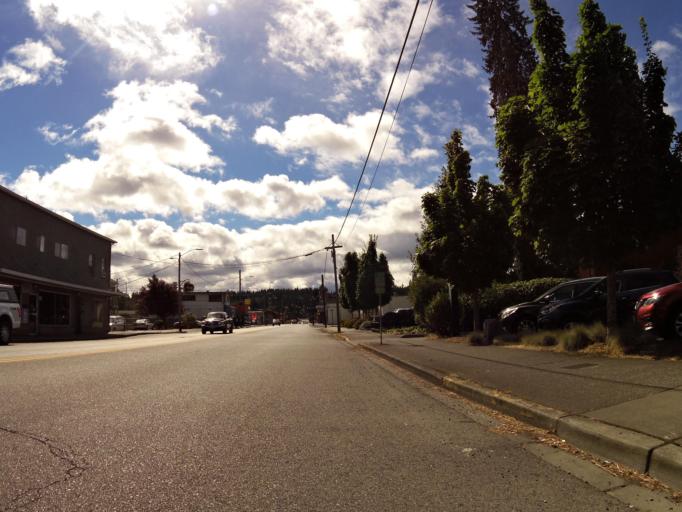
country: US
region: Washington
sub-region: Mason County
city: Shelton
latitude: 47.2144
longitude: -123.0999
